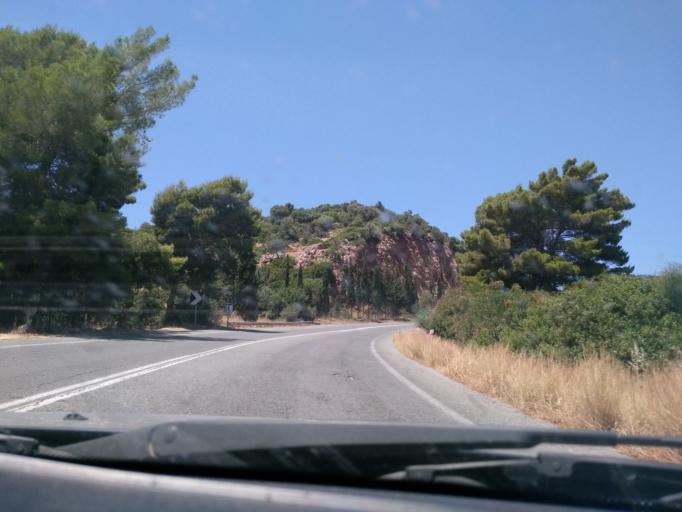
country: GR
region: Crete
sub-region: Nomos Rethymnis
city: Zoniana
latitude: 35.4018
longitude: 24.8587
